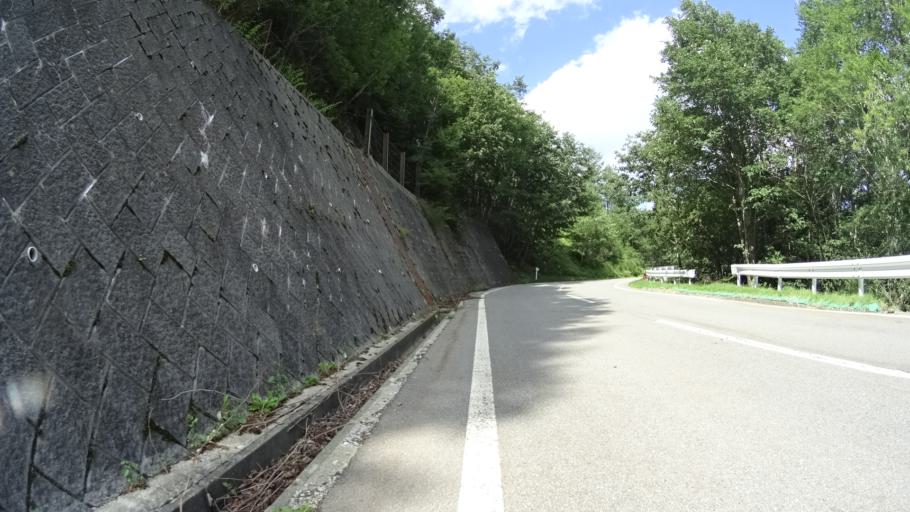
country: JP
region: Nagano
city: Saku
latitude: 36.0543
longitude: 138.3938
